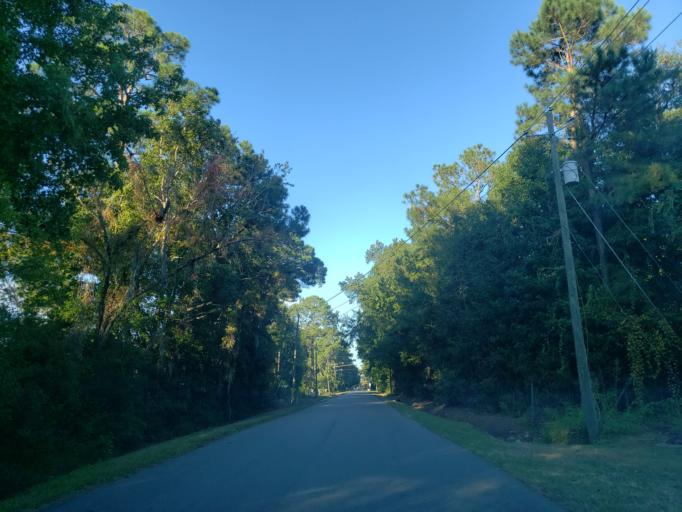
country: US
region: Georgia
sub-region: Chatham County
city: Isle of Hope
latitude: 31.9938
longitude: -81.0701
